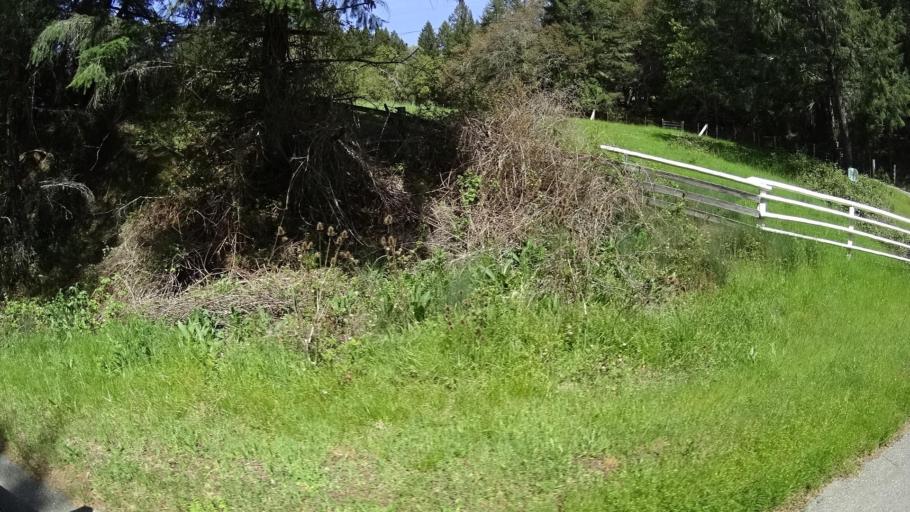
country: US
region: California
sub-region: Humboldt County
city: Redway
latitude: 40.3154
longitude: -123.6593
